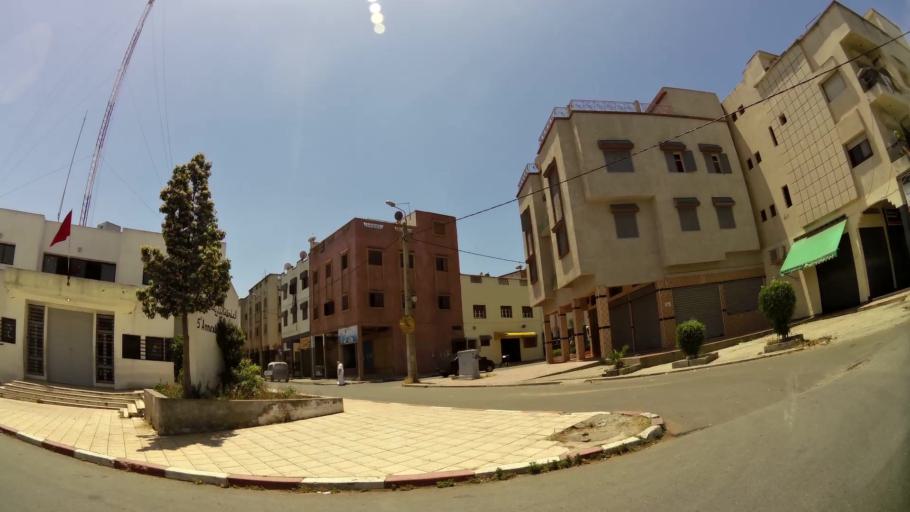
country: MA
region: Gharb-Chrarda-Beni Hssen
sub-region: Kenitra Province
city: Kenitra
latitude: 34.2624
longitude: -6.6199
